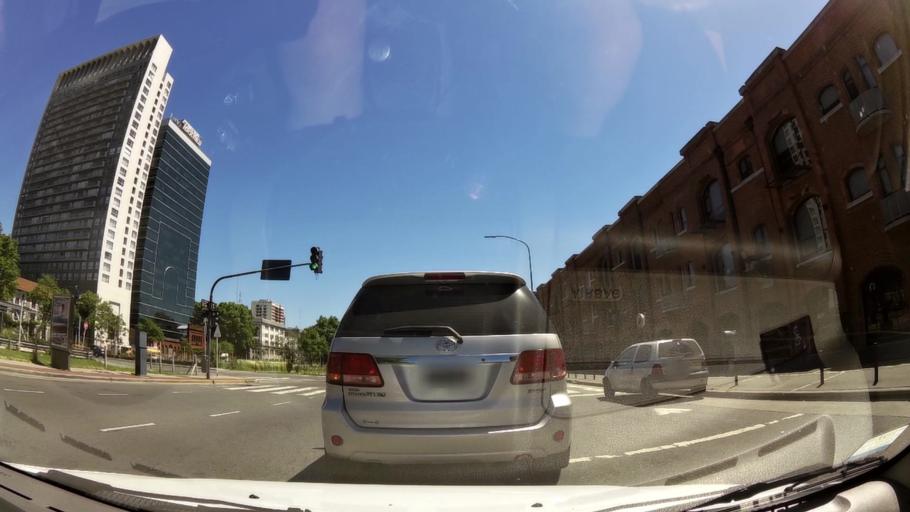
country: AR
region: Buenos Aires F.D.
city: Buenos Aires
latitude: -34.6171
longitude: -58.3659
